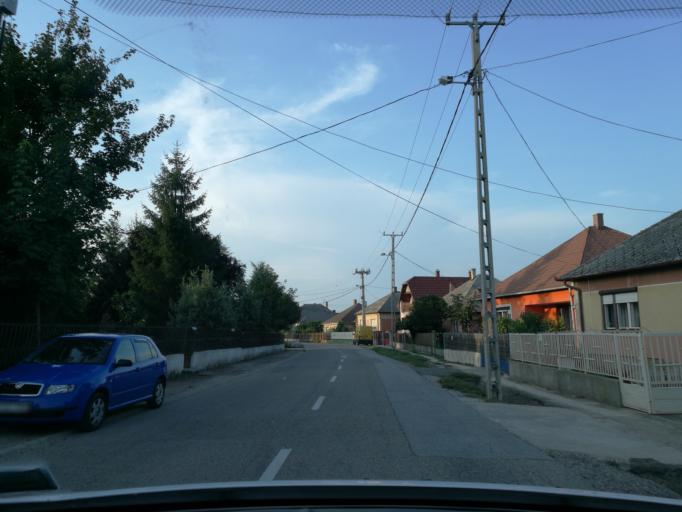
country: HU
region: Szabolcs-Szatmar-Bereg
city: Nyirpazony
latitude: 47.9523
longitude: 21.8052
